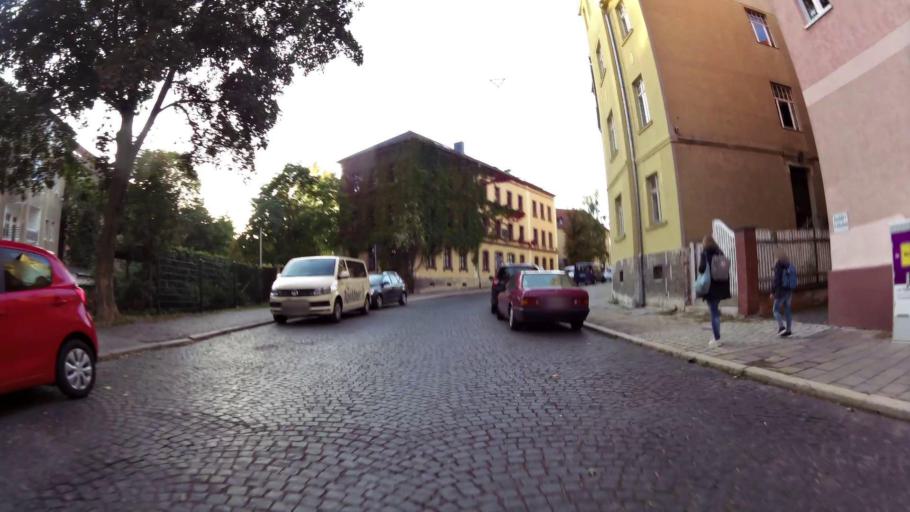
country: DE
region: Thuringia
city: Weimar
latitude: 50.9857
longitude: 11.3210
